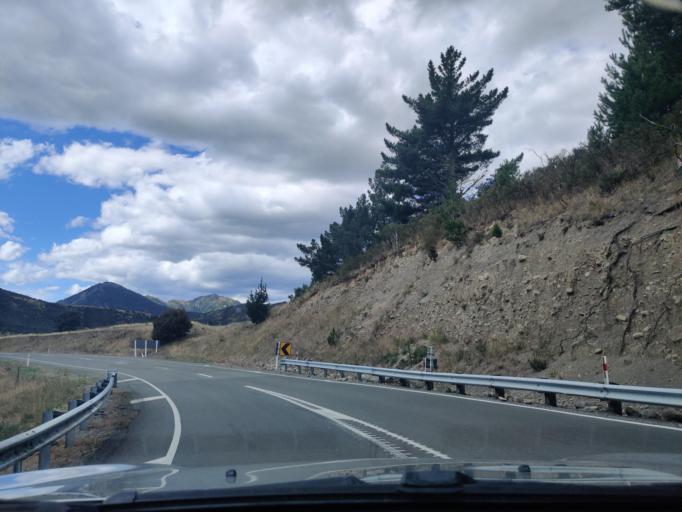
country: NZ
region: Canterbury
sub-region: Hurunui District
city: Amberley
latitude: -42.5944
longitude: 172.5027
